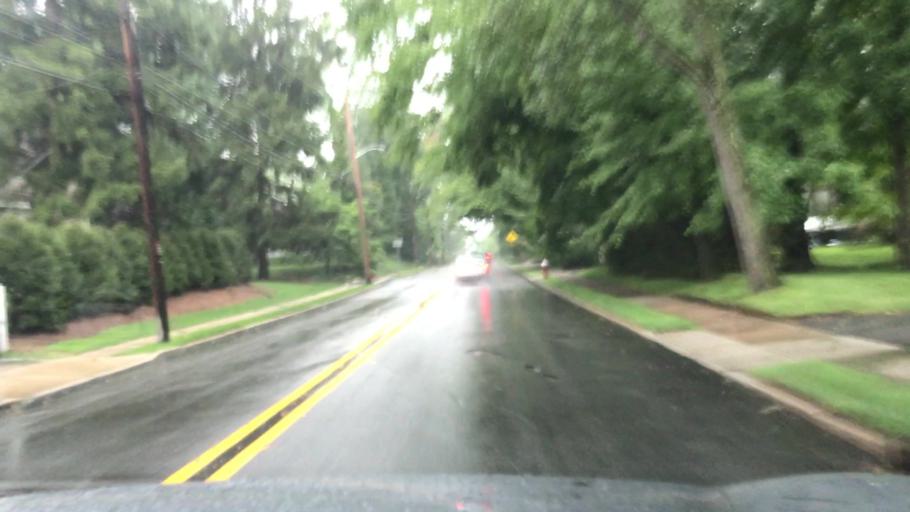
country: US
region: New Jersey
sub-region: Bergen County
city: Harrington Park
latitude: 40.9752
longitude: -73.9762
